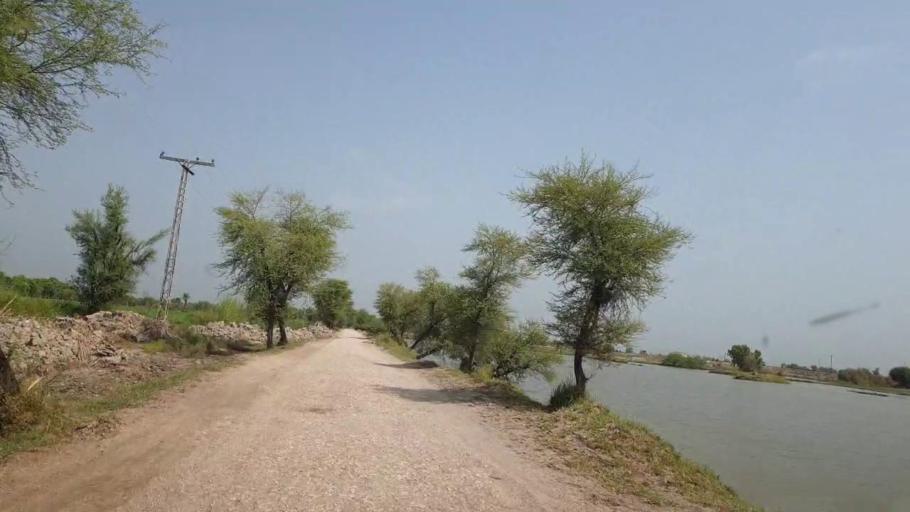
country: PK
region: Sindh
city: Lakhi
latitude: 27.8743
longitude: 68.6590
